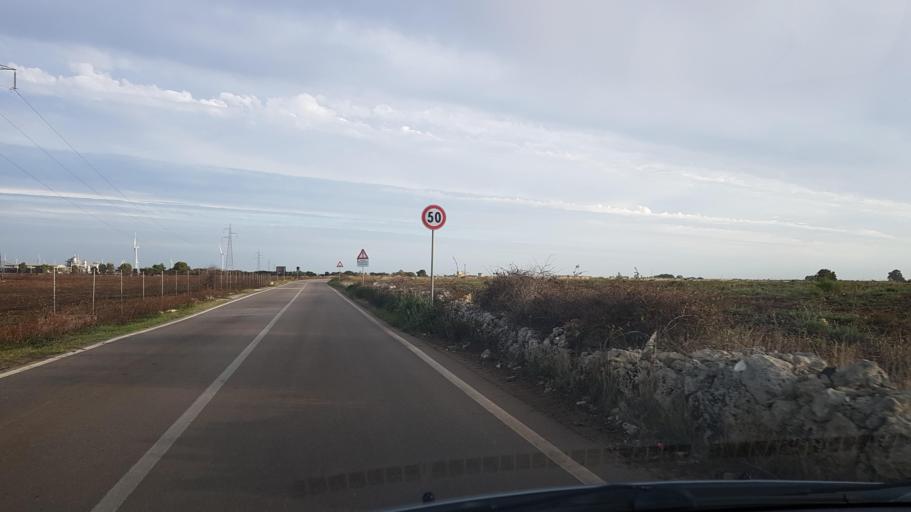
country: IT
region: Apulia
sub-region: Provincia di Lecce
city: Trepuzzi
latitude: 40.4476
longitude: 18.1074
